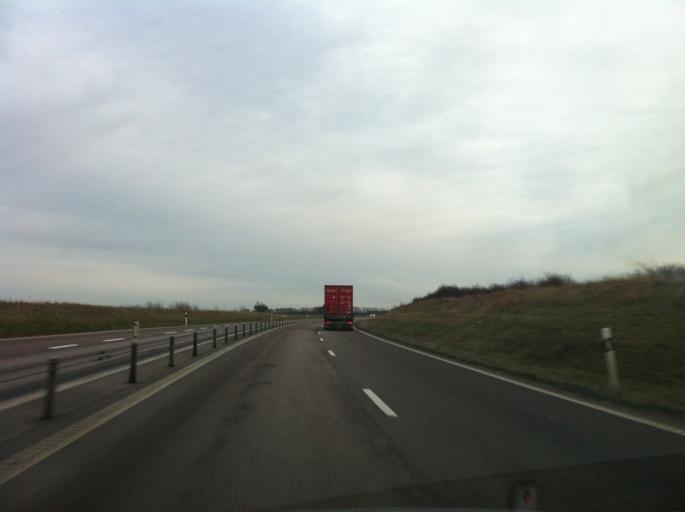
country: SE
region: Skane
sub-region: Hoganas Kommun
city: Hoganas
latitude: 56.1621
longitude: 12.5889
